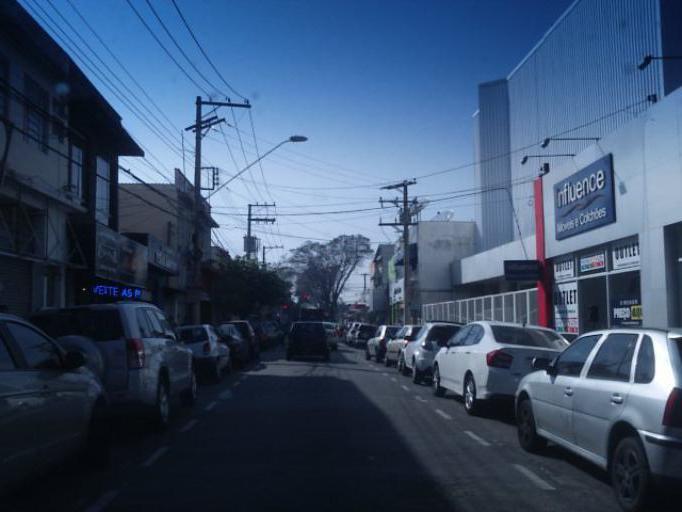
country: BR
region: Sao Paulo
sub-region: Sao Jose Dos Campos
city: Sao Jose dos Campos
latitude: -23.1838
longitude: -45.8841
